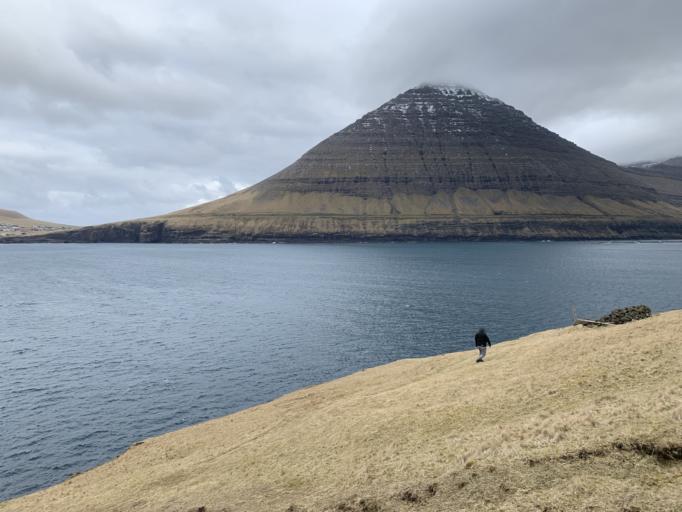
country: FO
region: Nordoyar
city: Klaksvik
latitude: 62.3549
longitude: -6.5812
